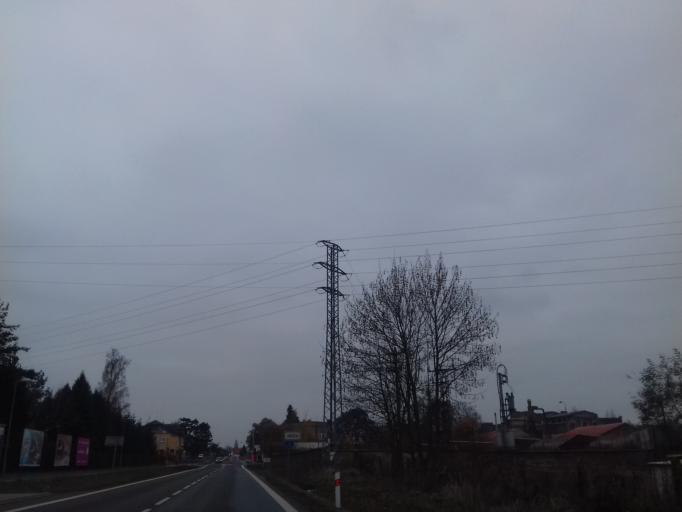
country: CZ
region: Plzensky
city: Zbuch
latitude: 49.6856
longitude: 13.2379
